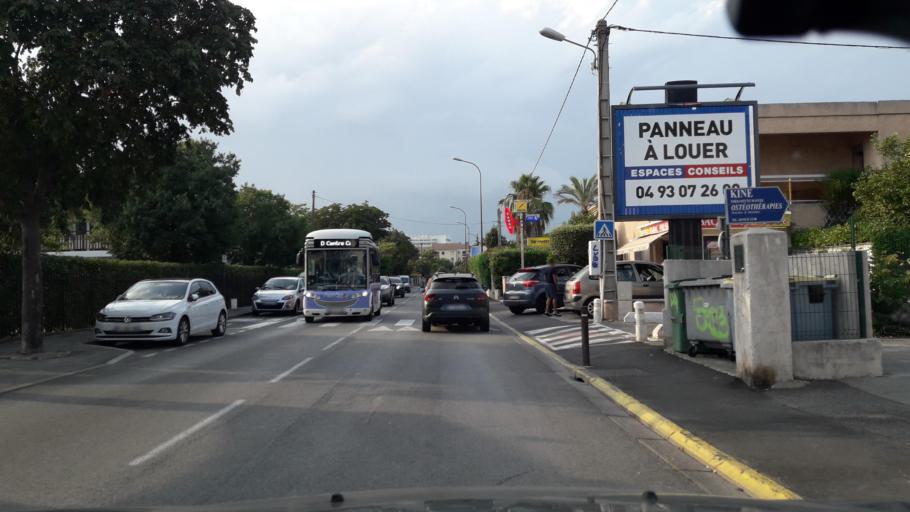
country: FR
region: Provence-Alpes-Cote d'Azur
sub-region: Departement du Var
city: Frejus
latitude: 43.4332
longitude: 6.7544
